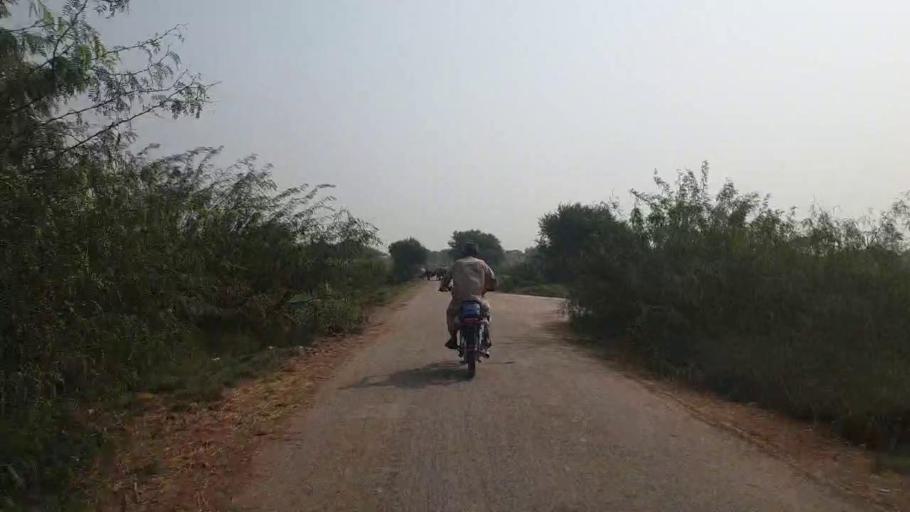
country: PK
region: Sindh
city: Tando Muhammad Khan
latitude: 25.2442
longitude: 68.5689
